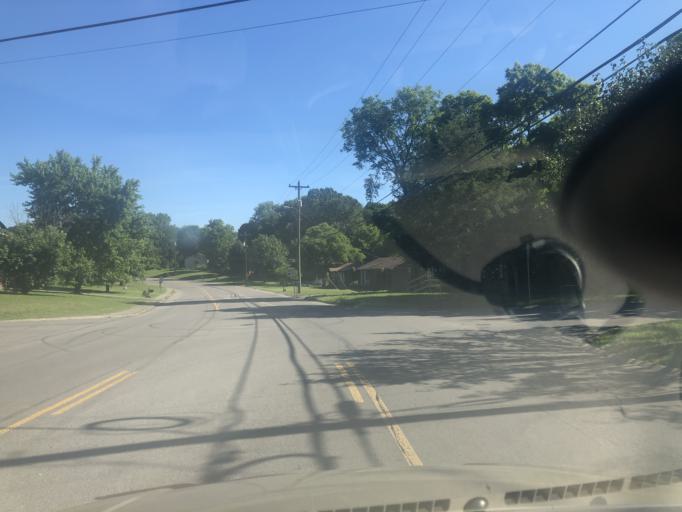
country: US
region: Tennessee
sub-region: Davidson County
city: Lakewood
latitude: 36.2465
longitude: -86.6694
